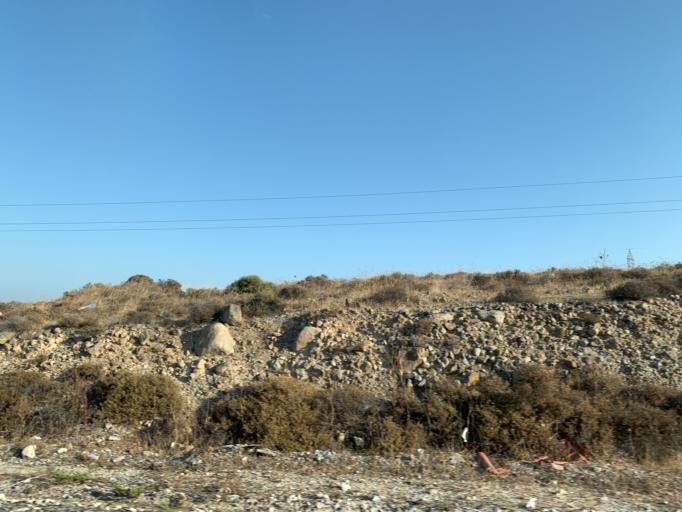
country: TR
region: Izmir
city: Alacati
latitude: 38.2768
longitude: 26.4183
